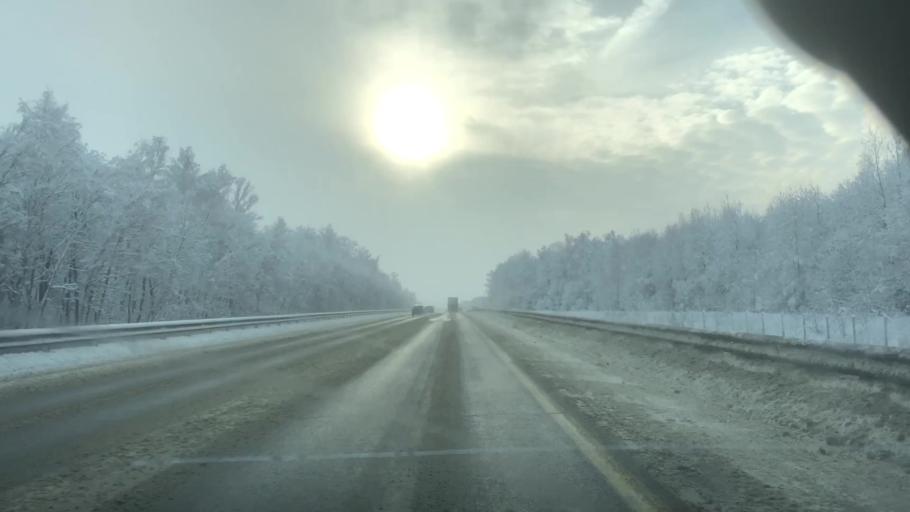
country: RU
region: Tula
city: Venev
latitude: 54.5261
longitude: 38.1680
